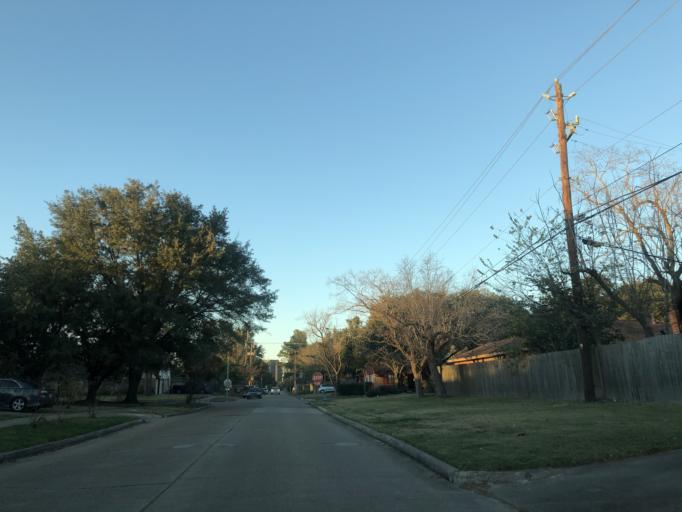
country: US
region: Texas
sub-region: Harris County
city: Bellaire
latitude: 29.6878
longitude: -95.5177
